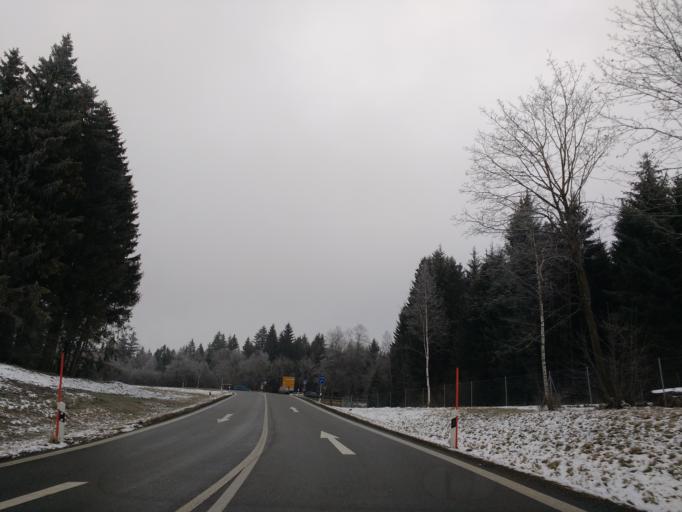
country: DE
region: Bavaria
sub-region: Swabia
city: Oy-Mittelberg
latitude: 47.6529
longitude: 10.4628
